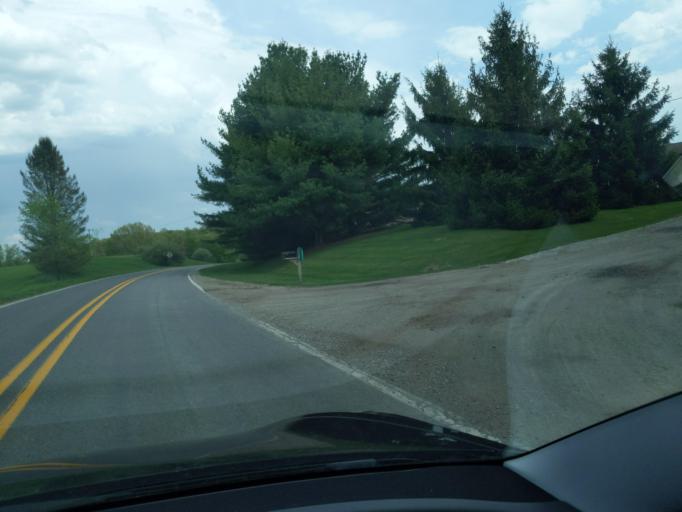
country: US
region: Michigan
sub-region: Ingham County
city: Stockbridge
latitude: 42.4314
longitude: -84.0728
